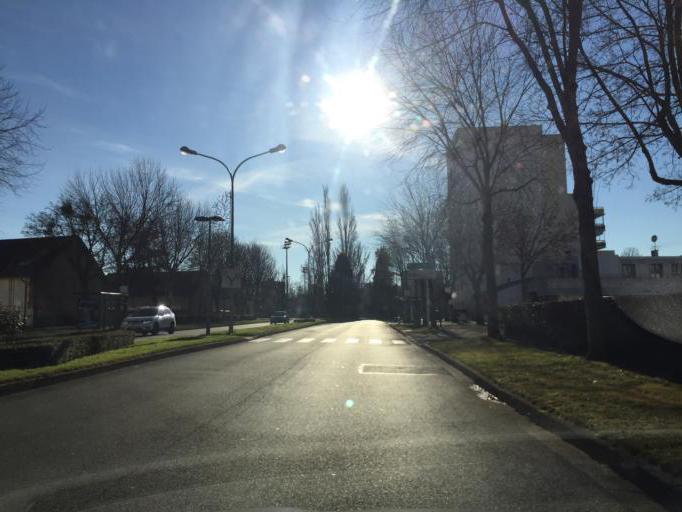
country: FR
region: Auvergne
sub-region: Departement de l'Allier
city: Vichy
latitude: 46.1372
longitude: 3.4158
